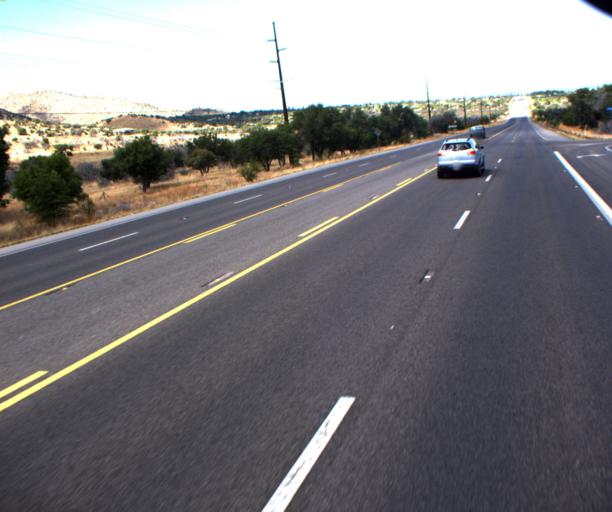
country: US
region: Arizona
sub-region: Cochise County
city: Sierra Vista Southeast
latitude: 31.4085
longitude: -110.2407
